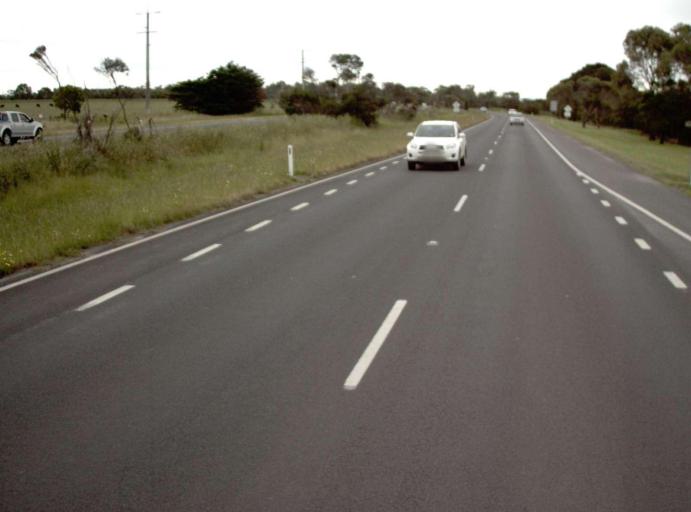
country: AU
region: Victoria
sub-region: Cardinia
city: Koo-Wee-Rup
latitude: -38.2221
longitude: 145.5091
